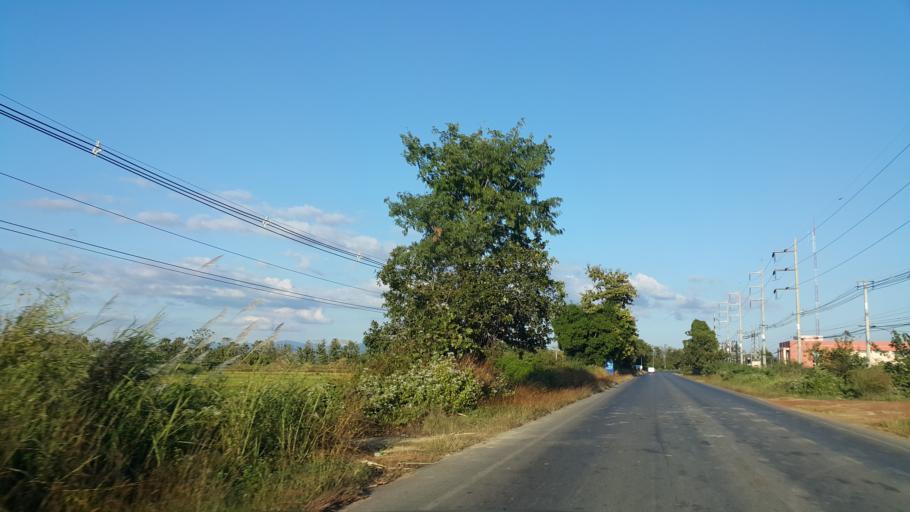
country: TH
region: Sukhothai
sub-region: Amphoe Si Satchanalai
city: Si Satchanalai
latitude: 17.5352
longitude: 99.7972
